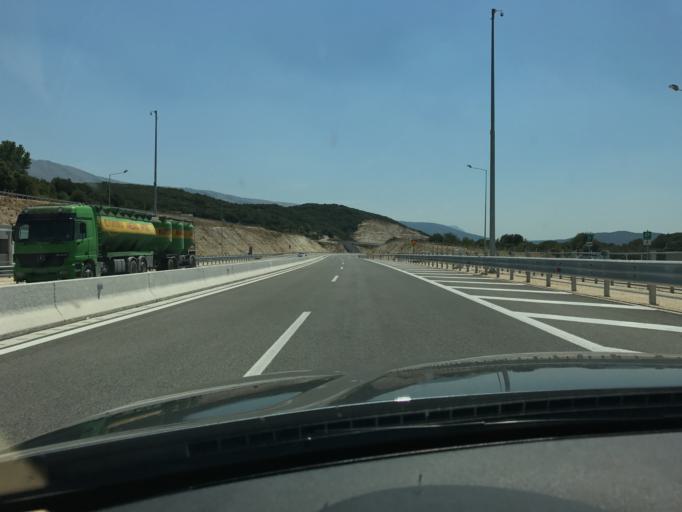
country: GR
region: Epirus
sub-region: Nomos Ioanninon
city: Agia Kyriaki
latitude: 39.4714
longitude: 20.8959
